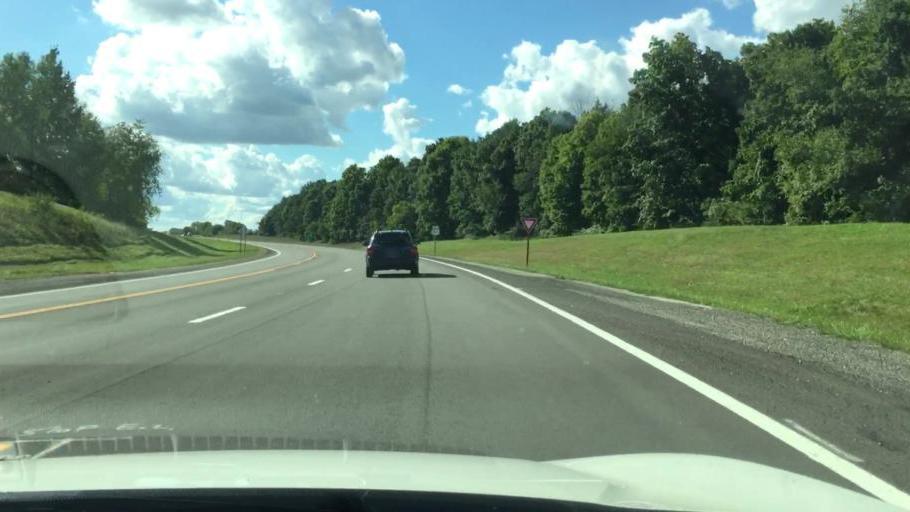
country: US
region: Ohio
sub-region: Clark County
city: Northridge
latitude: 39.9764
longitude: -83.7490
